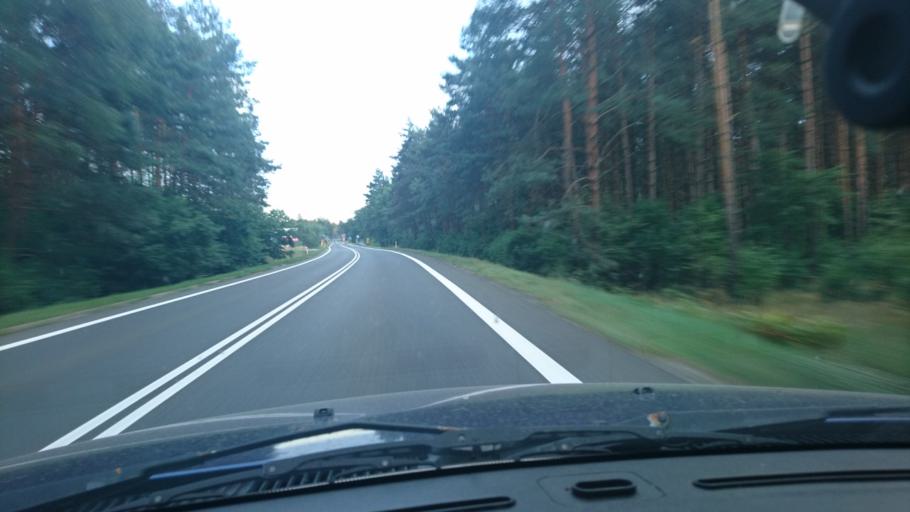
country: PL
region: Silesian Voivodeship
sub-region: Powiat tarnogorski
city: Tworog
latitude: 50.5903
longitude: 18.7013
